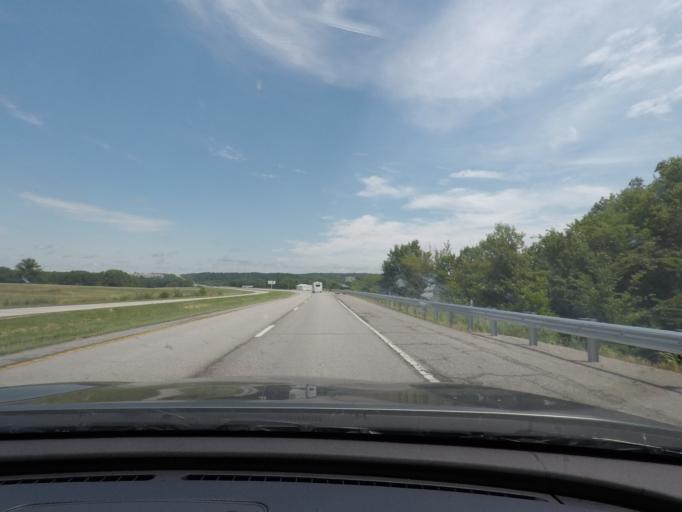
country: US
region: Missouri
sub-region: Saline County
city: Marshall
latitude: 38.9846
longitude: -93.1978
